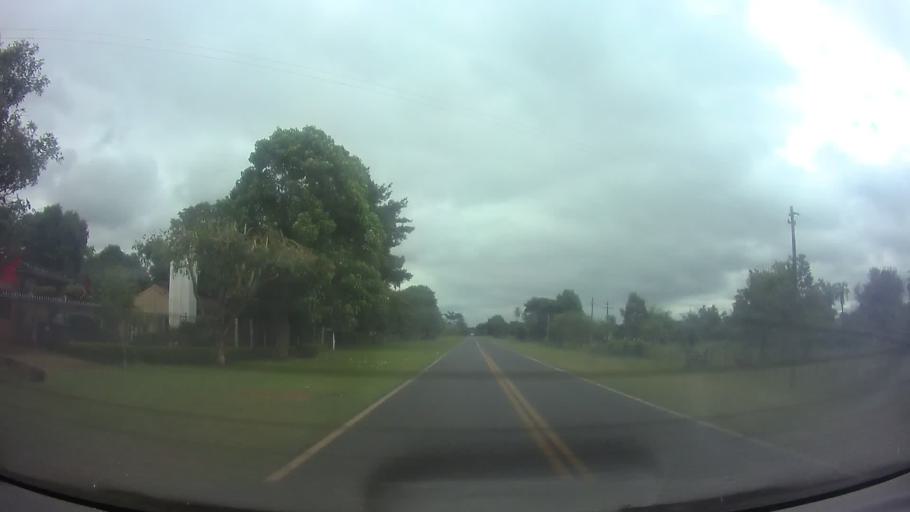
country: PY
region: Paraguari
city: Ybycui
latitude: -25.9822
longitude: -57.0700
